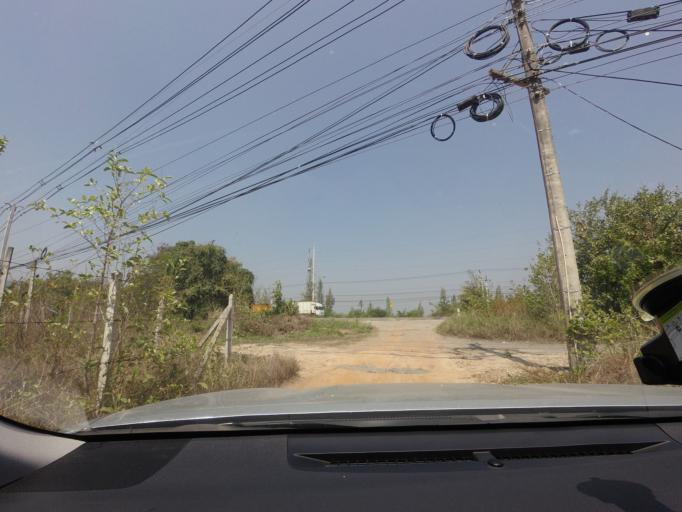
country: TH
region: Prachuap Khiri Khan
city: Prachuap Khiri Khan
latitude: 11.9339
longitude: 99.8152
